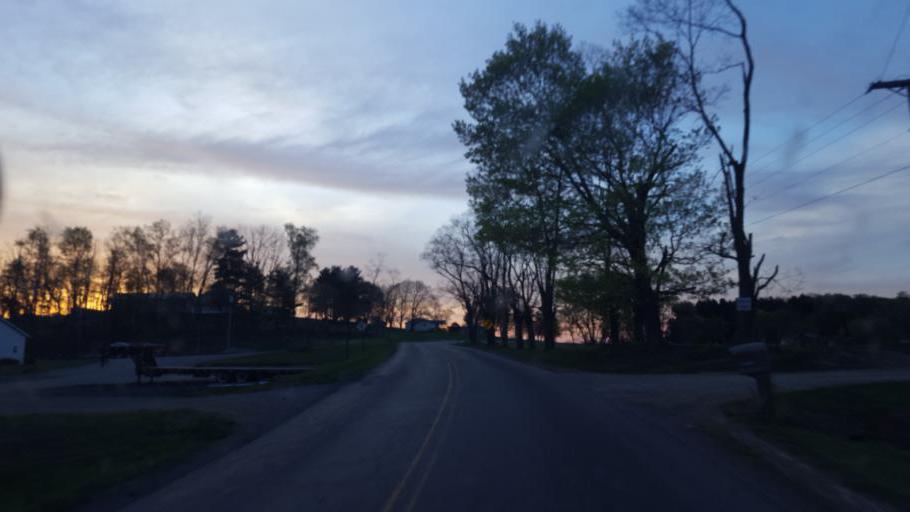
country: US
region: Ohio
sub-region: Knox County
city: Danville
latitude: 40.4541
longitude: -82.2796
